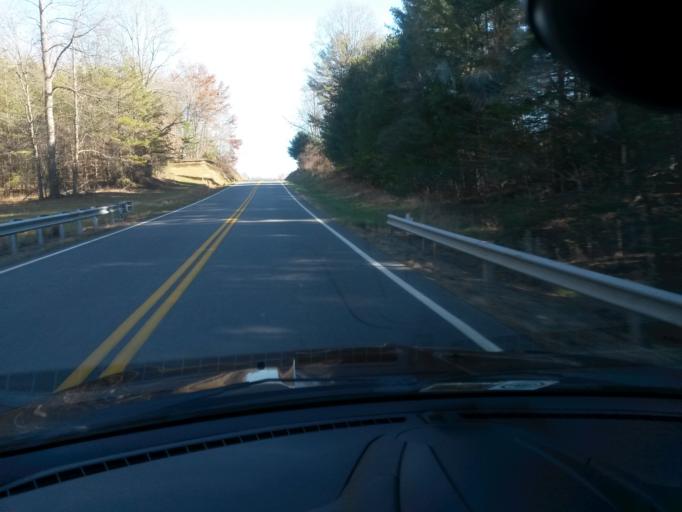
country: US
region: Virginia
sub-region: Patrick County
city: Patrick Springs
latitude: 36.7348
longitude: -80.2183
